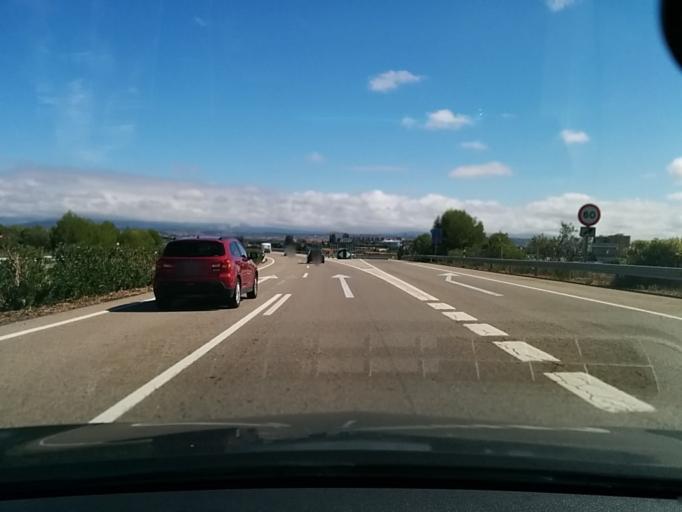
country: ES
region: Aragon
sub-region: Provincia de Huesca
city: Huesca
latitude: 42.1223
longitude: -0.4334
